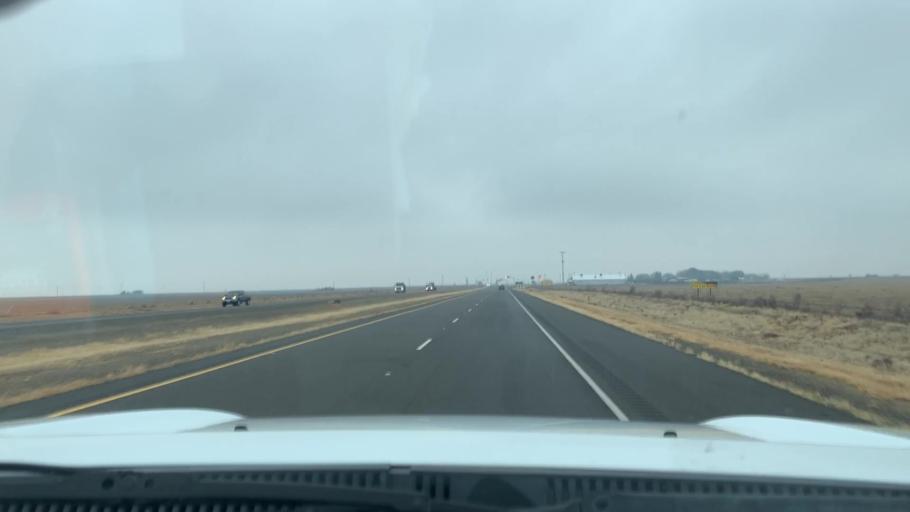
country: US
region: California
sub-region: Kern County
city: Lost Hills
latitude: 35.6147
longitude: -119.8768
